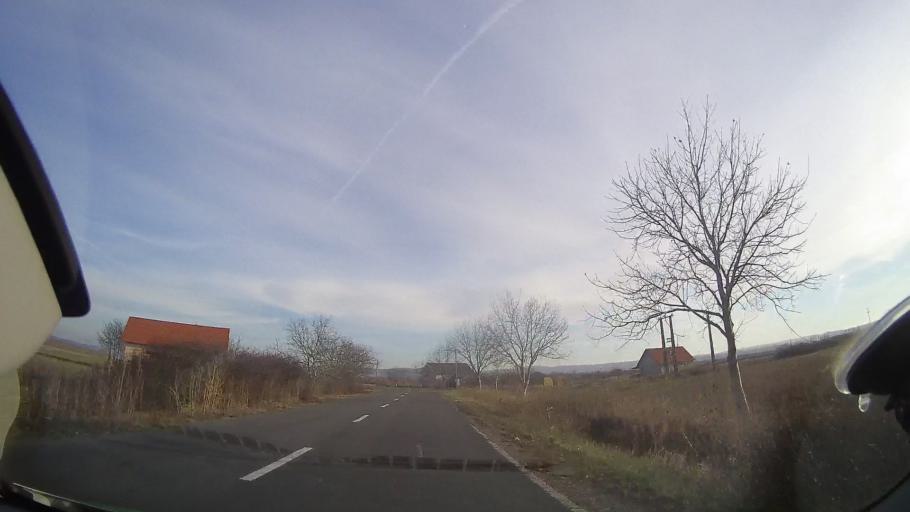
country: RO
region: Bihor
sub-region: Comuna Tileagd
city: Tileagd
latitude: 47.0648
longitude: 22.2231
